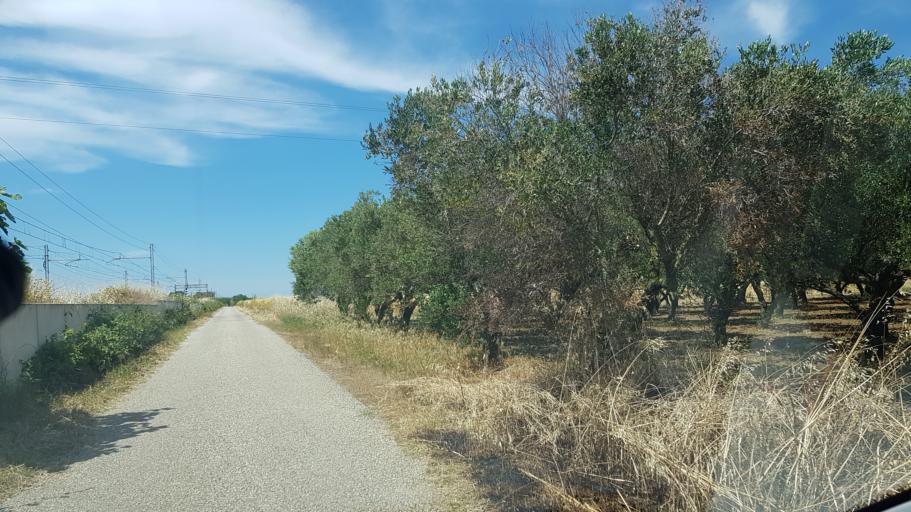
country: IT
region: Apulia
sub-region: Provincia di Brindisi
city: Tuturano
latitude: 40.5410
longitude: 17.9825
